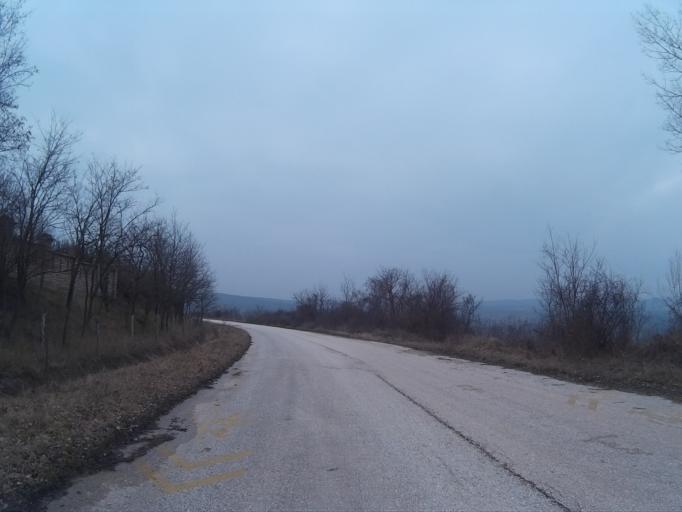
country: HU
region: Fejer
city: Many
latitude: 47.5341
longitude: 18.6019
